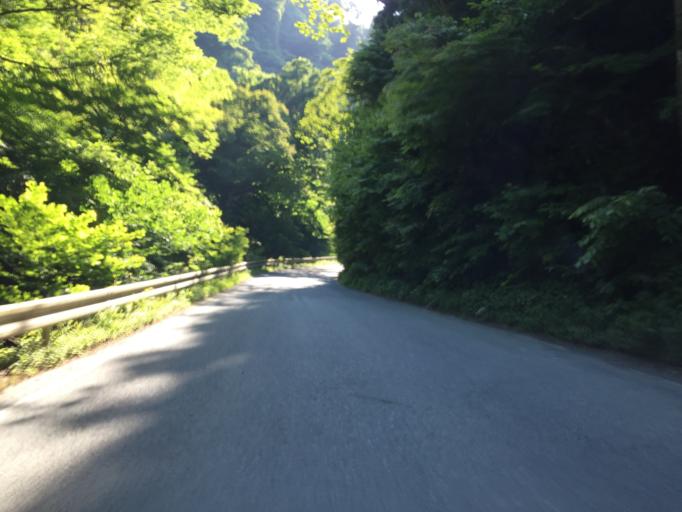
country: JP
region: Ibaraki
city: Kitaibaraki
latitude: 36.8662
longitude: 140.7082
